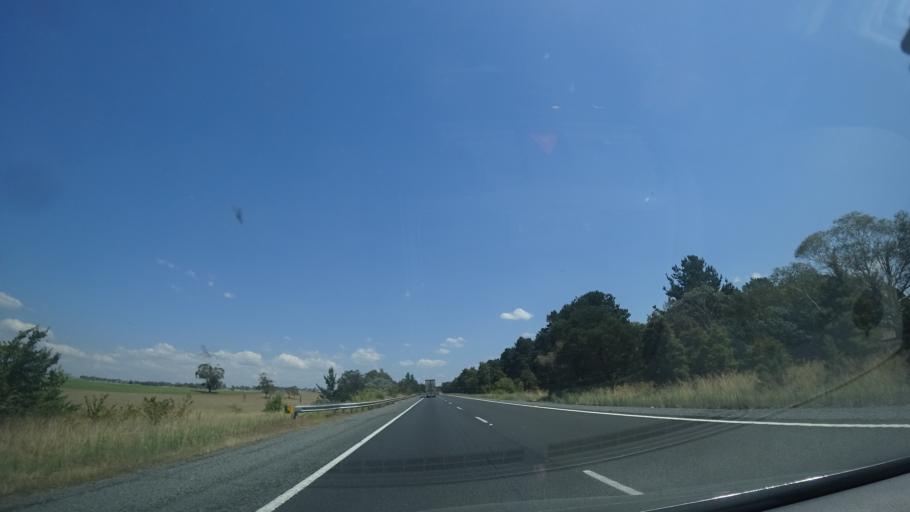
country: AU
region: New South Wales
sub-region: Wingecarribee
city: Moss Vale
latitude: -34.5502
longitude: 150.2687
